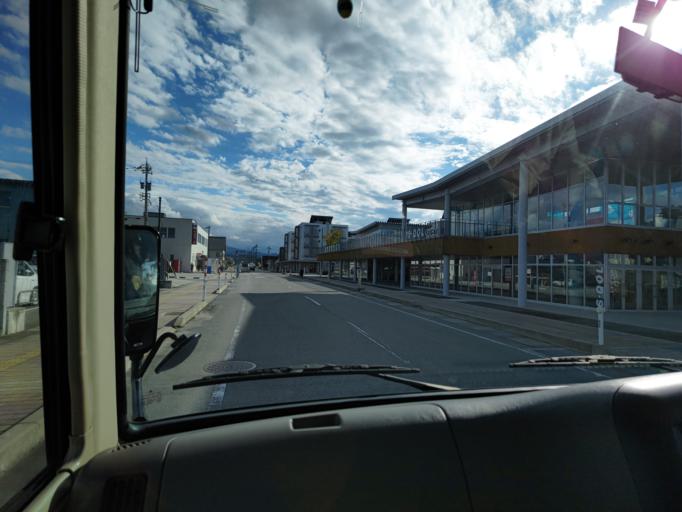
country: JP
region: Toyama
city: Nyuzen
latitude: 36.8790
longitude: 137.4466
